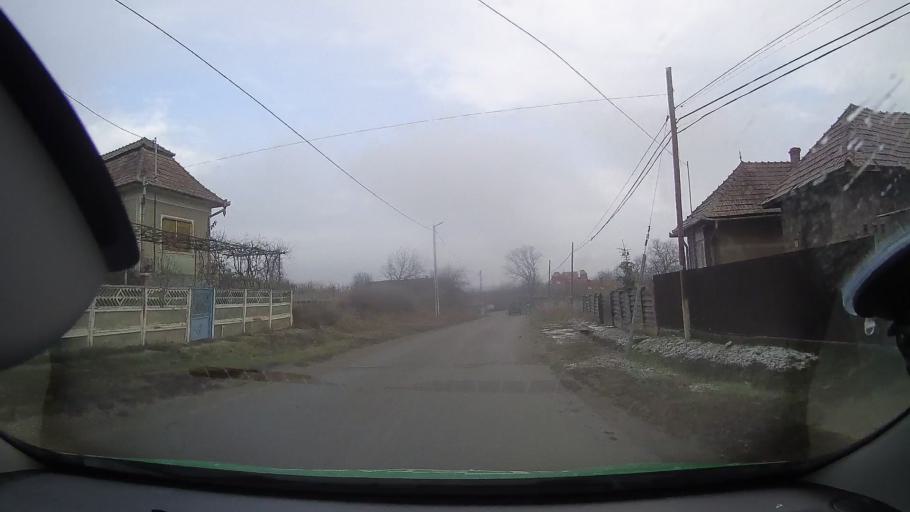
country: RO
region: Alba
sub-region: Comuna Noslac
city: Noslac
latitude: 46.4099
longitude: 23.9379
